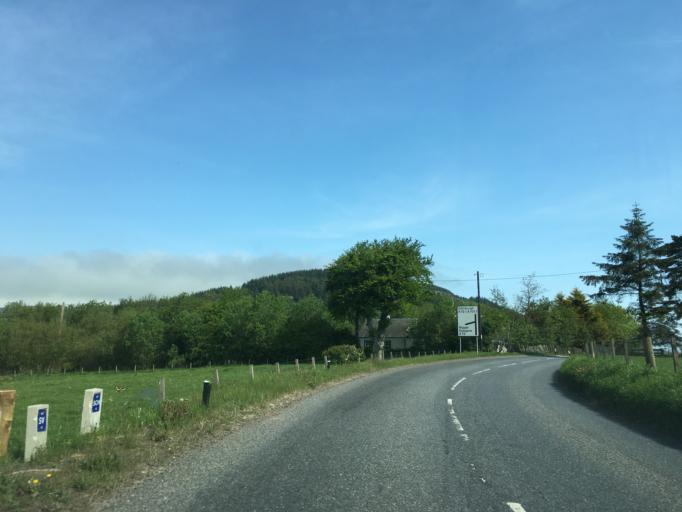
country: GB
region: Scotland
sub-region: South Lanarkshire
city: Biggar
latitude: 55.6526
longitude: -3.4341
